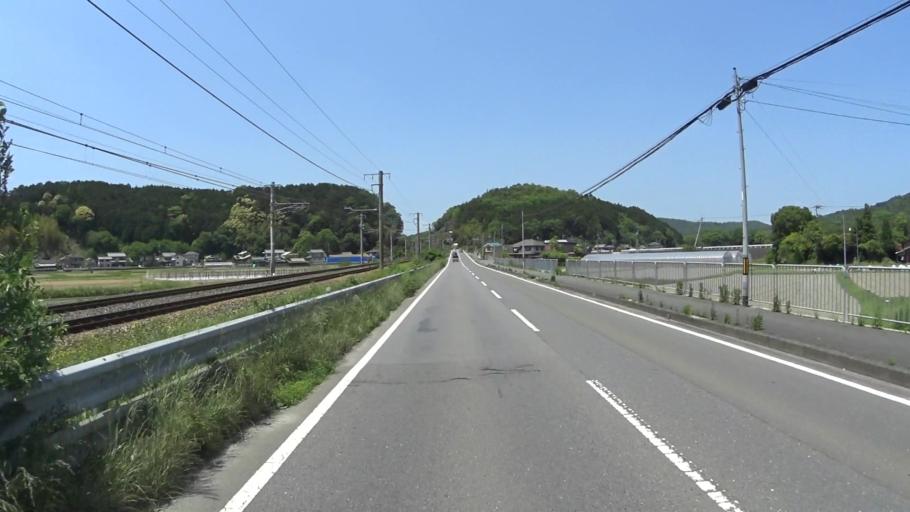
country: JP
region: Kyoto
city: Kameoka
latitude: 35.0784
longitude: 135.5193
